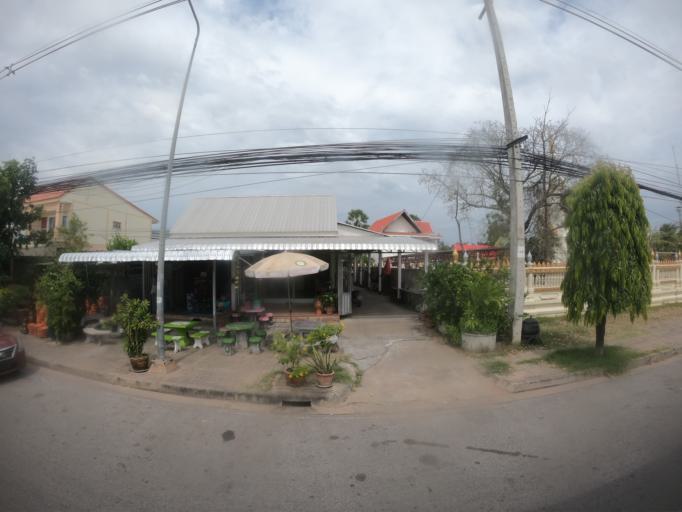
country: TH
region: Roi Et
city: Roi Et
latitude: 16.0564
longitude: 103.6374
